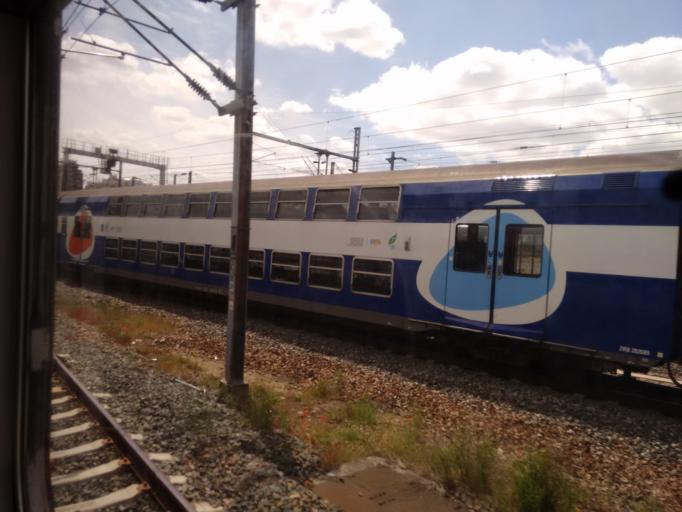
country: FR
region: Ile-de-France
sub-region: Paris
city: Saint-Ouen
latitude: 48.8933
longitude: 2.3562
